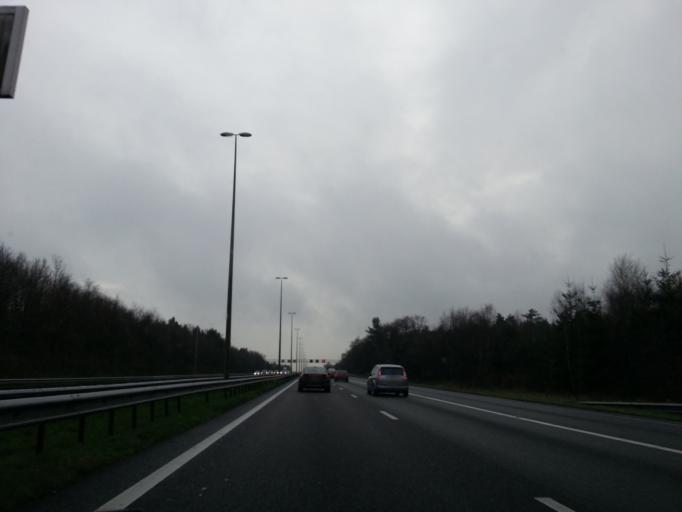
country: NL
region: Gelderland
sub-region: Gemeente Rozendaal
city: Rozendaal
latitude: 52.0777
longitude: 5.9462
